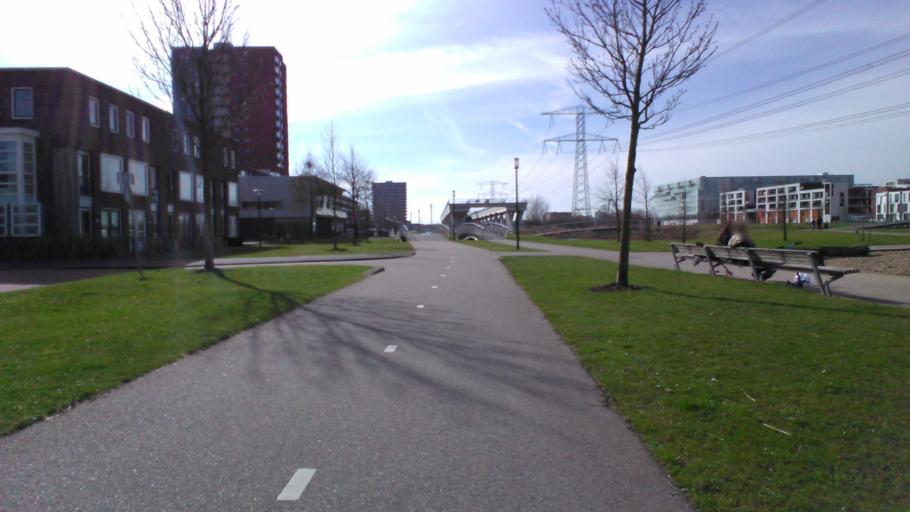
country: NL
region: South Holland
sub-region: Gemeente Capelle aan den IJssel
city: Capelle aan den IJssel
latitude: 51.9827
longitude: 4.5871
